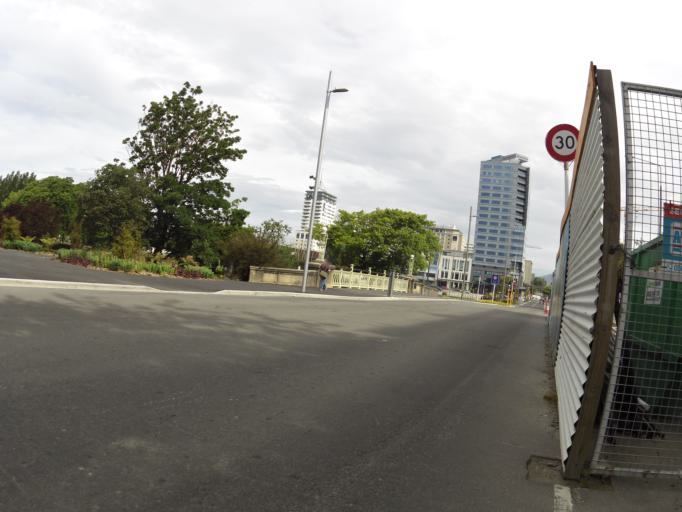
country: NZ
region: Canterbury
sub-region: Christchurch City
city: Christchurch
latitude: -43.5269
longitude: 172.6366
